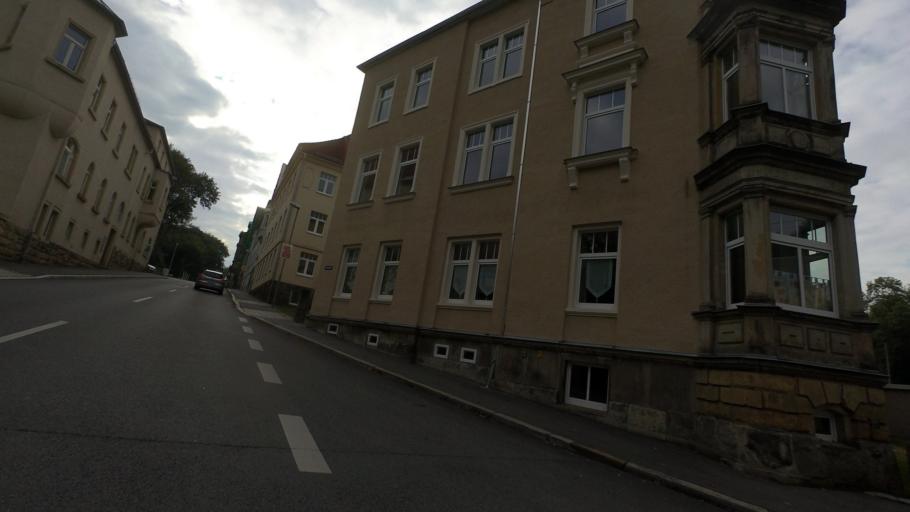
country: DE
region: Saxony
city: Sebnitz
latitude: 50.9772
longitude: 14.2810
